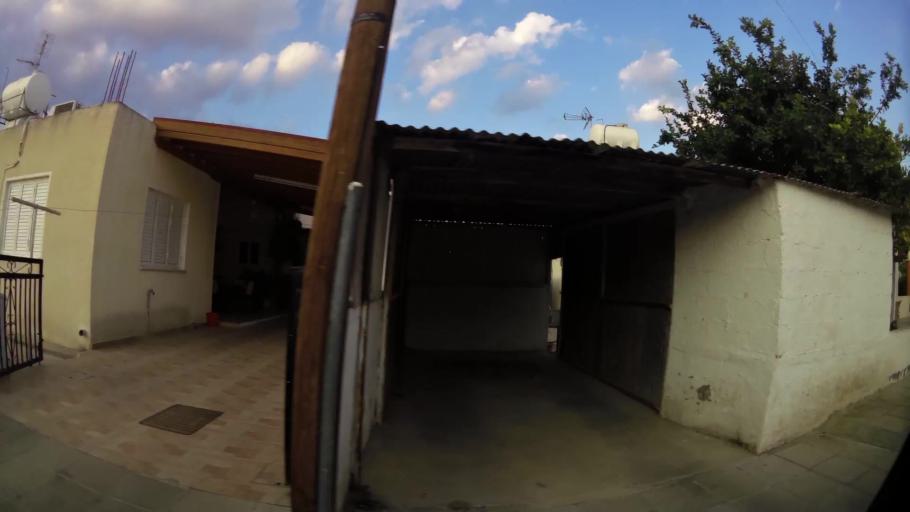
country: CY
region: Larnaka
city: Meneou
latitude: 34.8627
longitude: 33.5865
